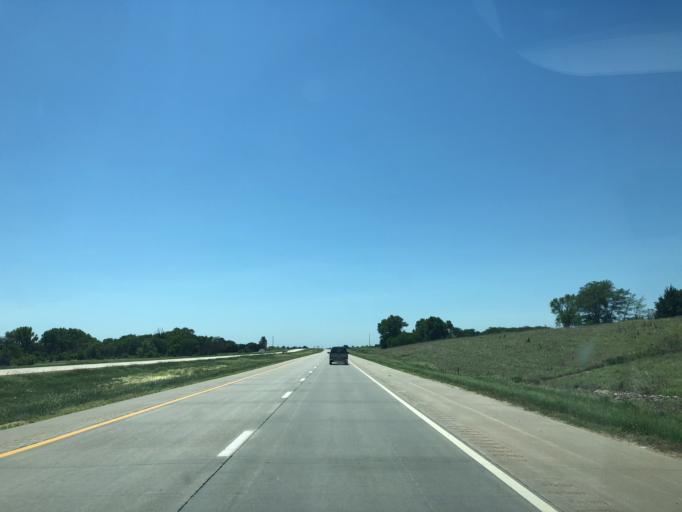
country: US
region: Kansas
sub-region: Cloud County
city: Concordia
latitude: 39.6587
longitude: -97.6605
